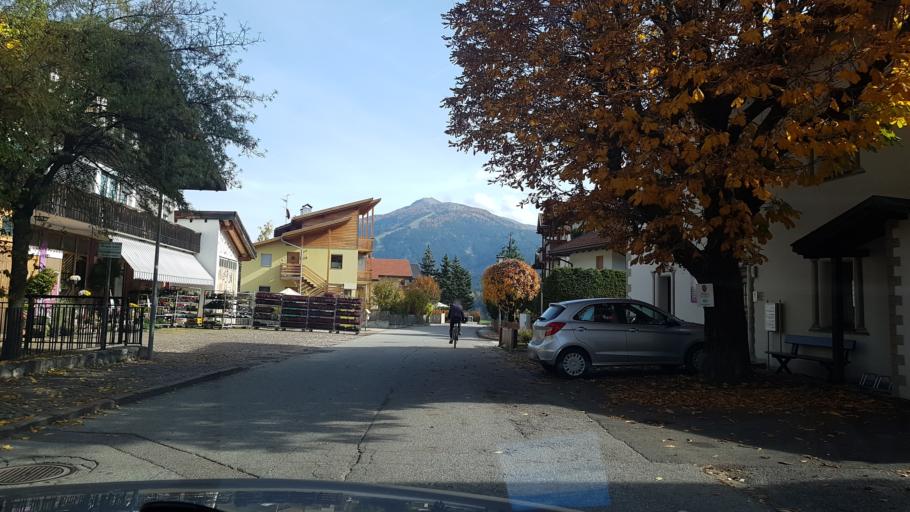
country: IT
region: Trentino-Alto Adige
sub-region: Bolzano
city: San Candido
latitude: 46.7317
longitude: 12.2850
